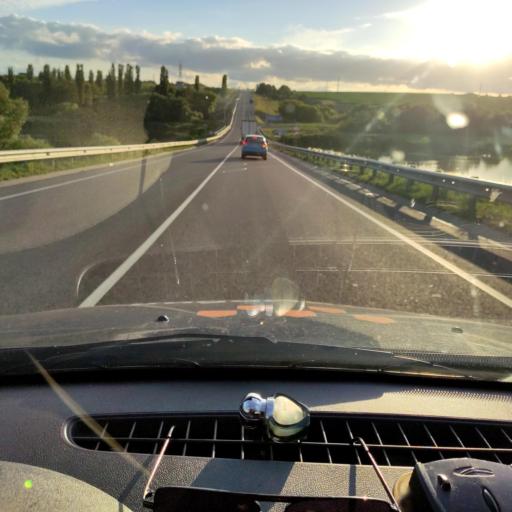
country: RU
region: Voronezj
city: Nizhnedevitsk
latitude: 51.5646
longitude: 38.3687
